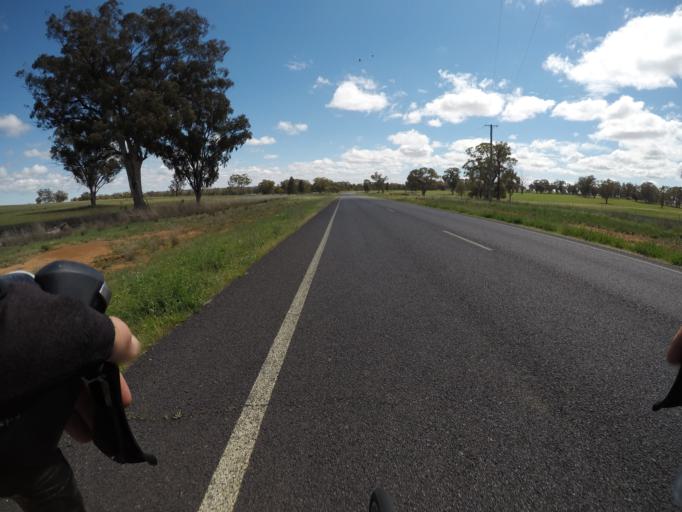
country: AU
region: New South Wales
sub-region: Dubbo Municipality
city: Dubbo
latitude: -32.5004
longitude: 148.5535
